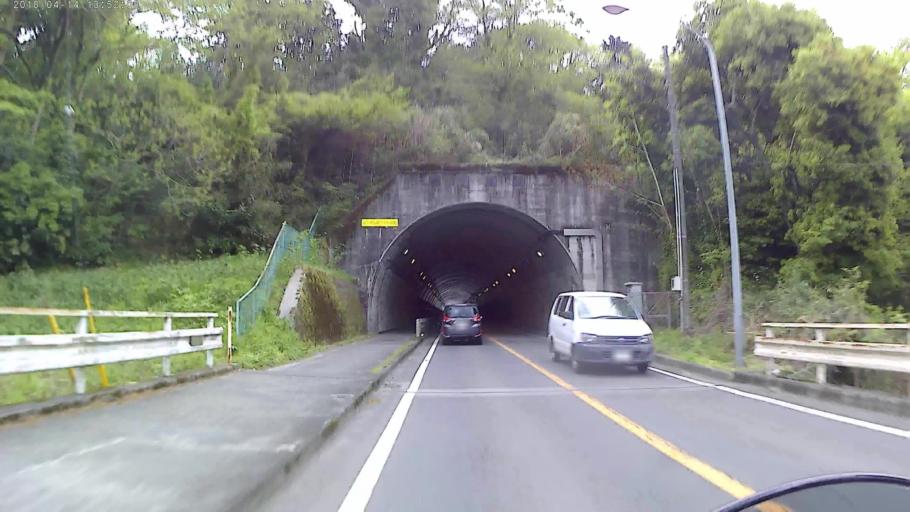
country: JP
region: Kanagawa
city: Odawara
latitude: 35.3241
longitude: 139.1109
